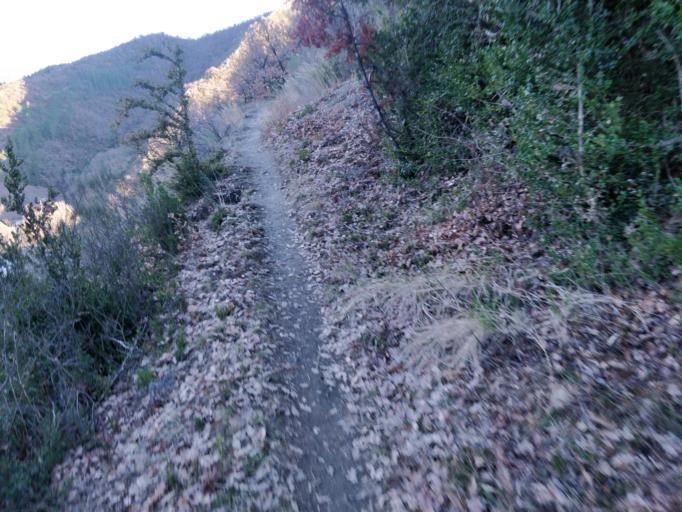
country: FR
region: Provence-Alpes-Cote d'Azur
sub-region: Departement des Alpes-de-Haute-Provence
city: Digne-les-Bains
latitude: 44.1019
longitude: 6.2475
